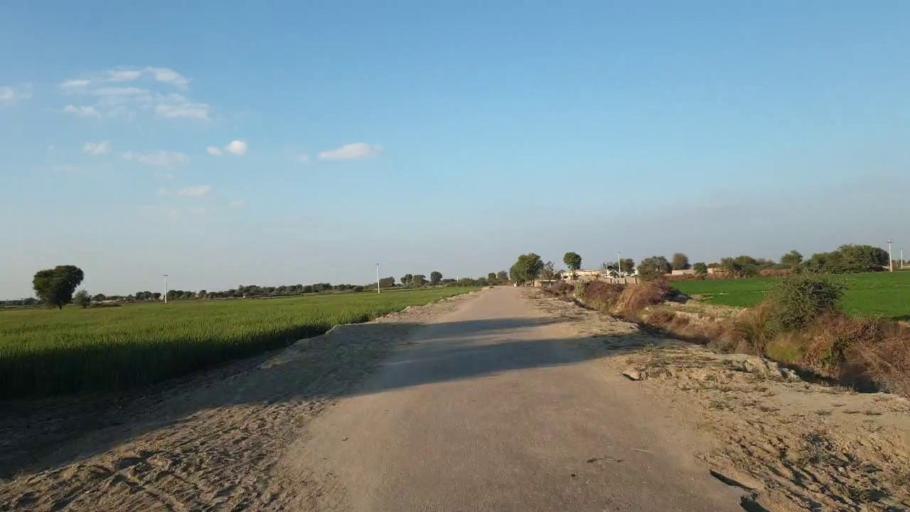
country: PK
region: Sindh
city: Shahpur Chakar
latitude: 26.1469
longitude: 68.5461
